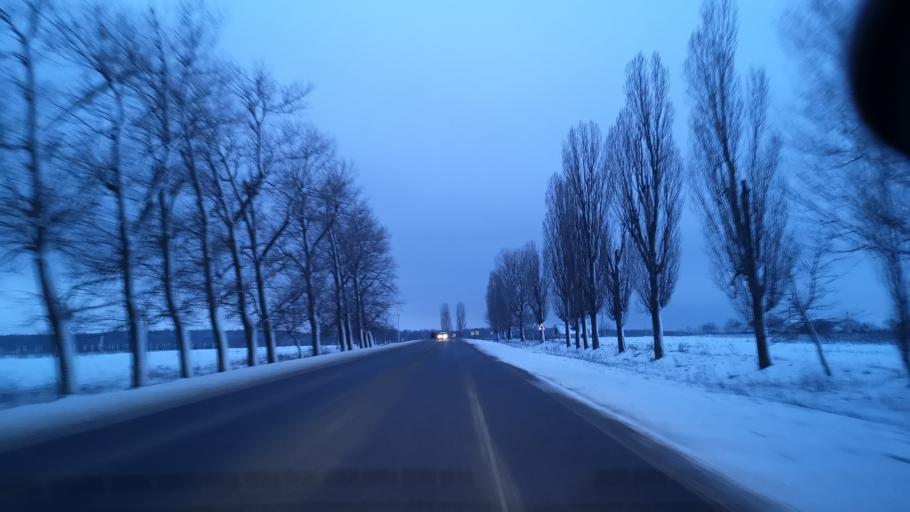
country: MD
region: Rezina
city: Rezina
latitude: 47.7364
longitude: 28.8812
